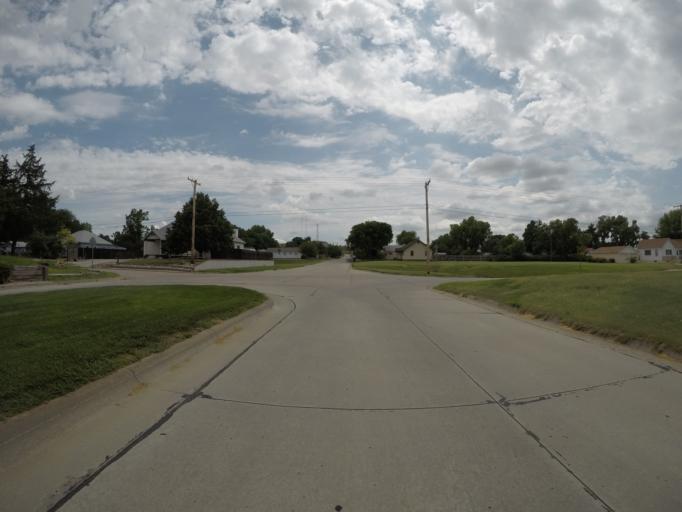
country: US
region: Kansas
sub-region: Rawlins County
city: Atwood
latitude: 39.8039
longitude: -101.0422
